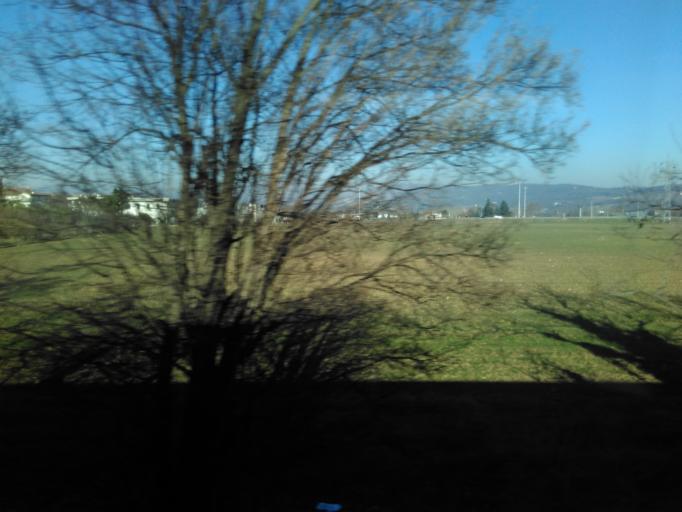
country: IT
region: Veneto
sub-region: Provincia di Verona
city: Montorio
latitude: 45.4249
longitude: 11.0617
